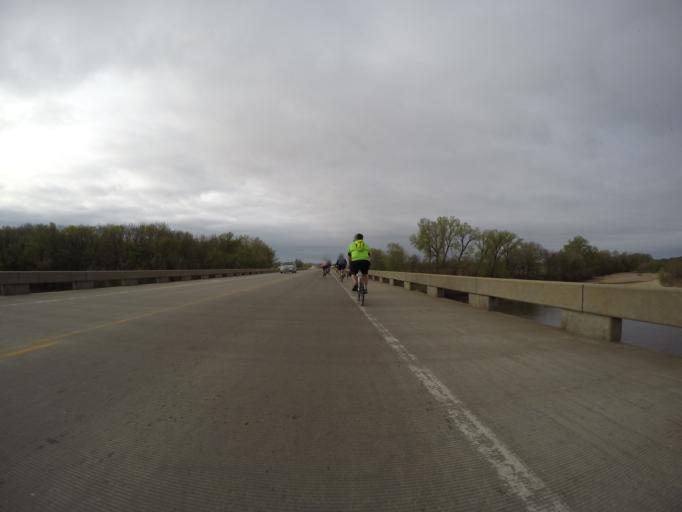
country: US
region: Kansas
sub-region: Pottawatomie County
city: Wamego
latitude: 39.1968
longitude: -96.3052
